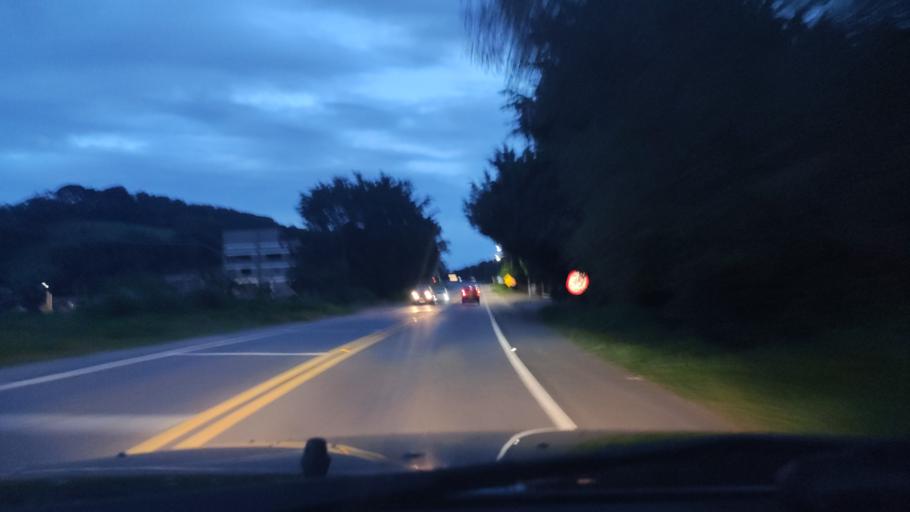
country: BR
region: Sao Paulo
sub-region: Socorro
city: Socorro
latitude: -22.5717
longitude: -46.5345
